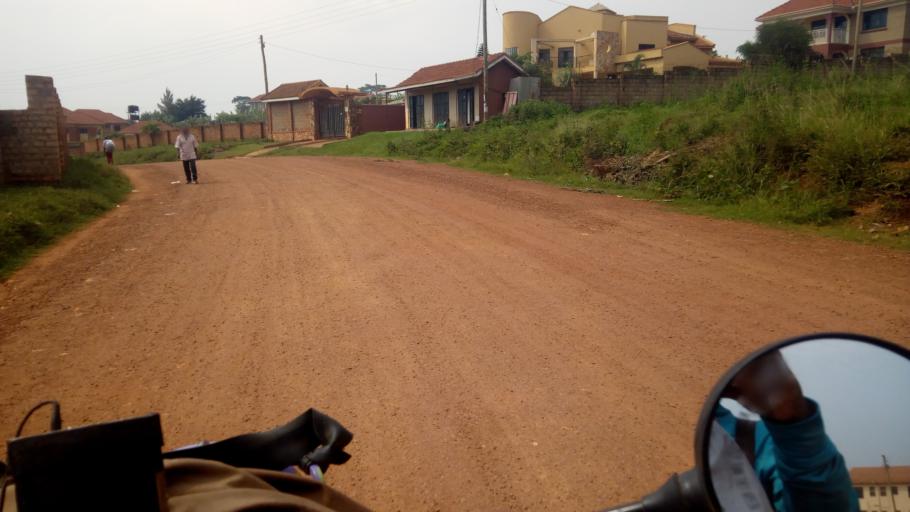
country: UG
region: Central Region
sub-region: Wakiso District
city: Kireka
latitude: 0.3151
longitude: 32.6537
